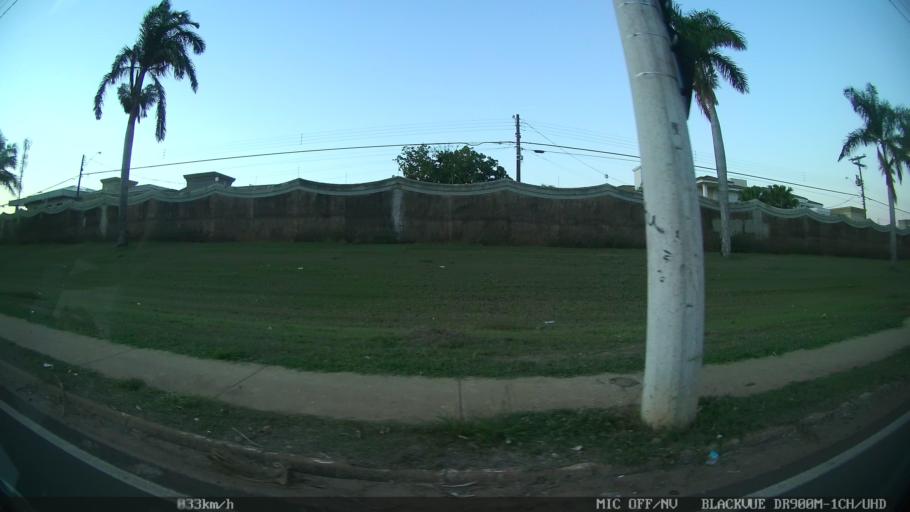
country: BR
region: Sao Paulo
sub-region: Sao Jose Do Rio Preto
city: Sao Jose do Rio Preto
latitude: -20.8110
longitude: -49.3504
